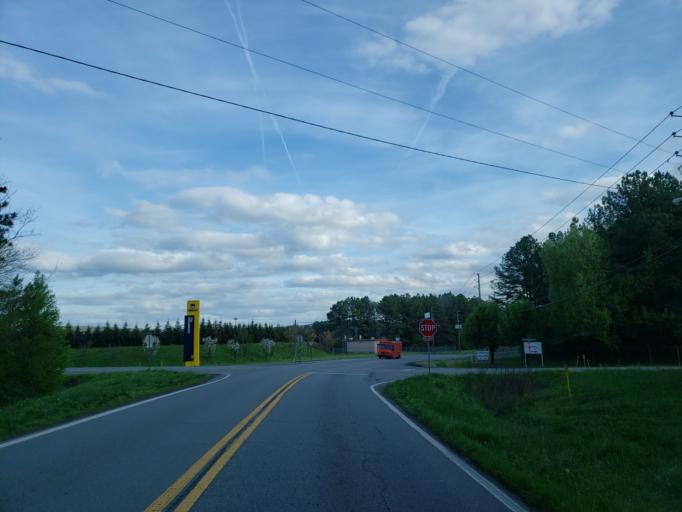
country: US
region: Georgia
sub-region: Bartow County
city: Cartersville
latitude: 34.2379
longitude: -84.8061
